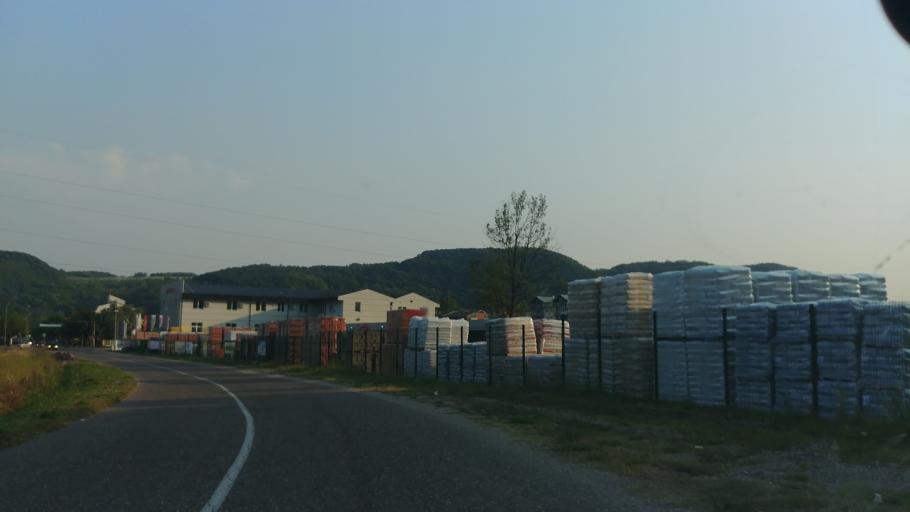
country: BA
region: Republika Srpska
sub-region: Opstina Ugljevik
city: Ugljevik
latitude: 44.6970
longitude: 18.9926
